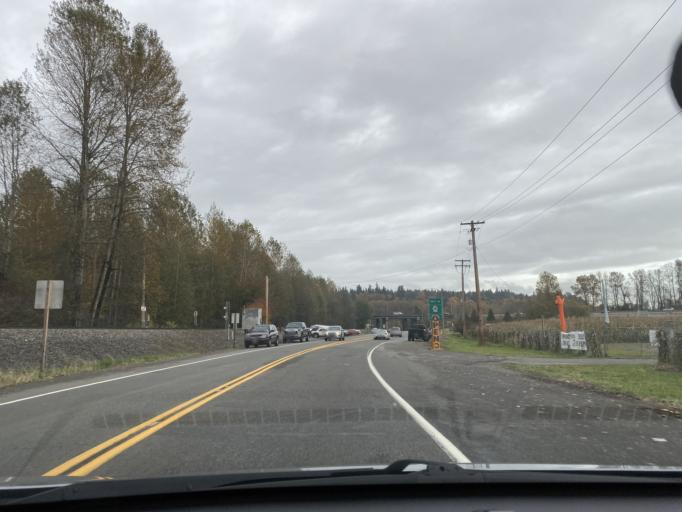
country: US
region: Washington
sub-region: King County
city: Lea Hill
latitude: 47.3009
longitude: -122.1849
